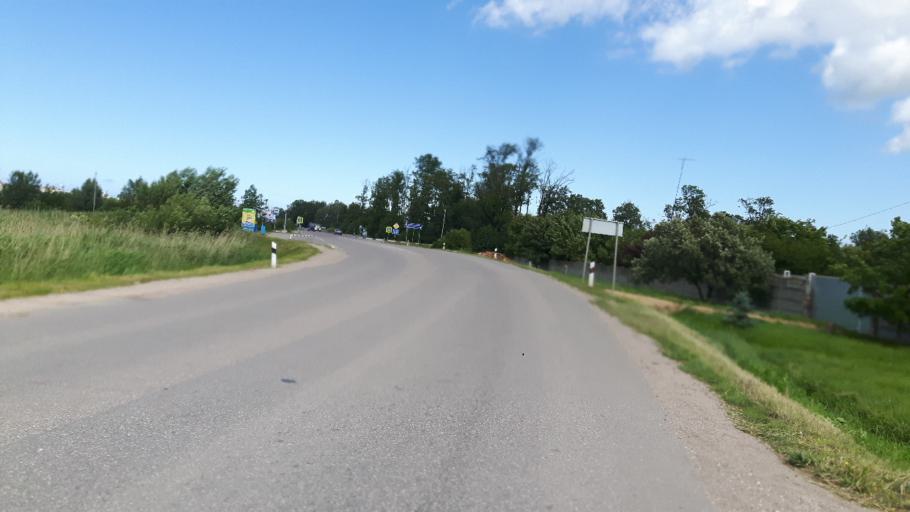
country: RU
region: Kaliningrad
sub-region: Zelenogradskiy Rayon
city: Zelenogradsk
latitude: 54.9442
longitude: 20.4667
